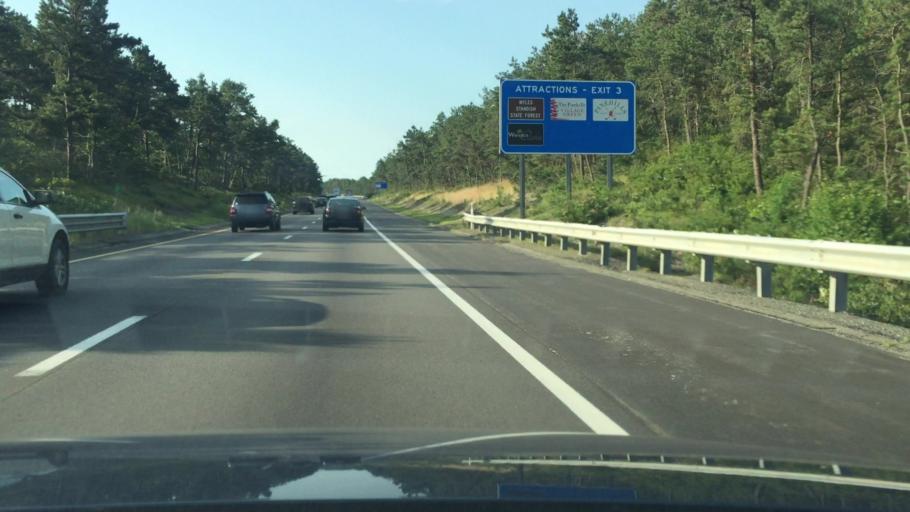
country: US
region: Massachusetts
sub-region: Plymouth County
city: Plymouth
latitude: 41.8887
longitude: -70.6122
